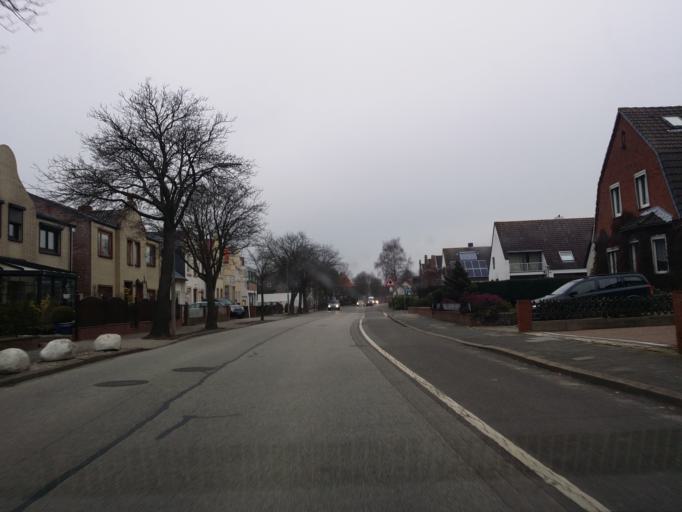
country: DE
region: Schleswig-Holstein
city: Burg auf Fehmarn
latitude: 54.4339
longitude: 11.2001
